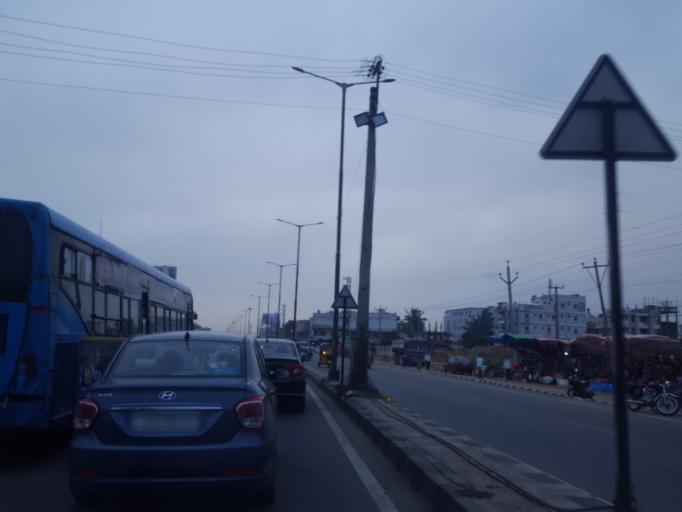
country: IN
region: Telangana
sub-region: Medak
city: Patancheru
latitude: 17.5299
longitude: 78.2610
